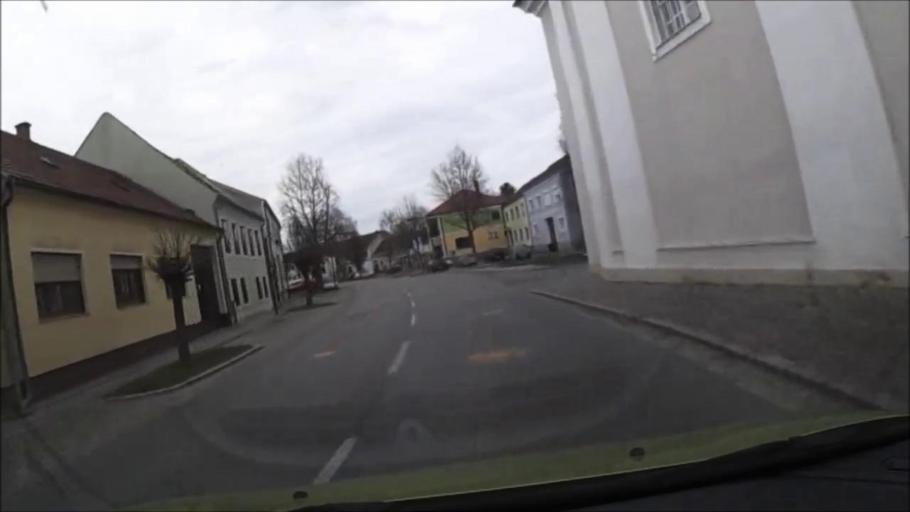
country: AT
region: Burgenland
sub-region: Eisenstadt-Umgebung
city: Leithaprodersdorf
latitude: 47.9388
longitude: 16.4723
